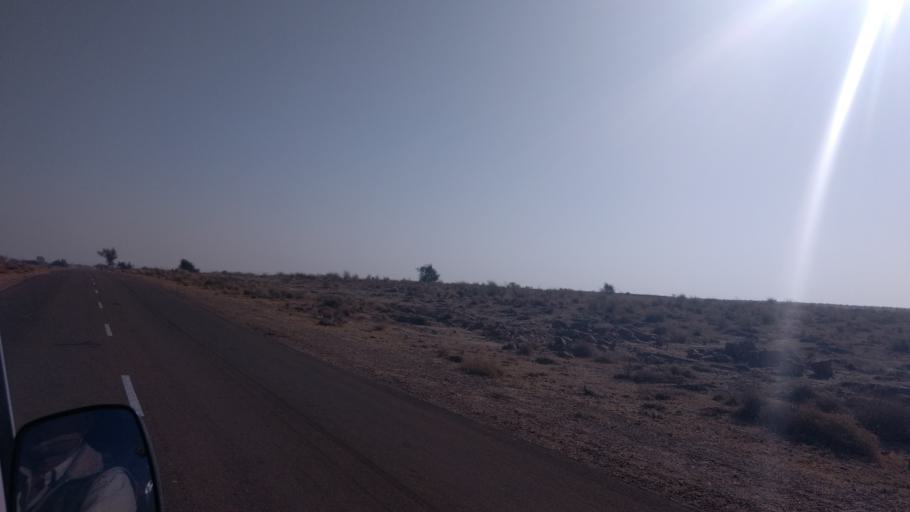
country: IN
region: Rajasthan
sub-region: Jaisalmer
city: Jaisalmer
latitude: 26.9101
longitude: 70.7491
